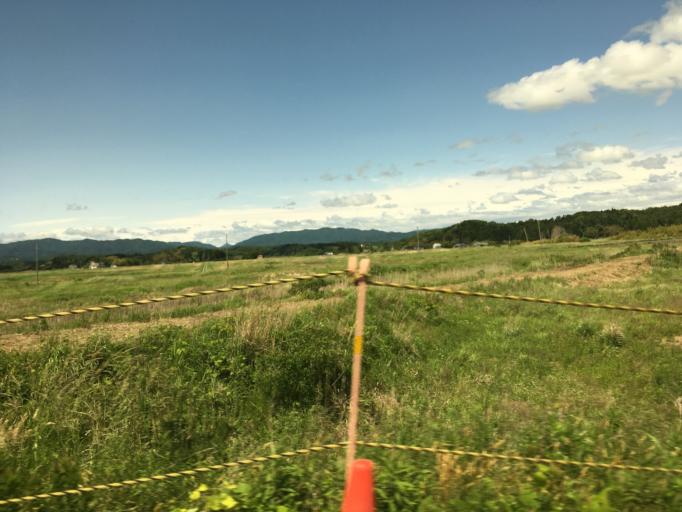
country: JP
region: Fukushima
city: Namie
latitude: 37.4623
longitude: 141.0307
